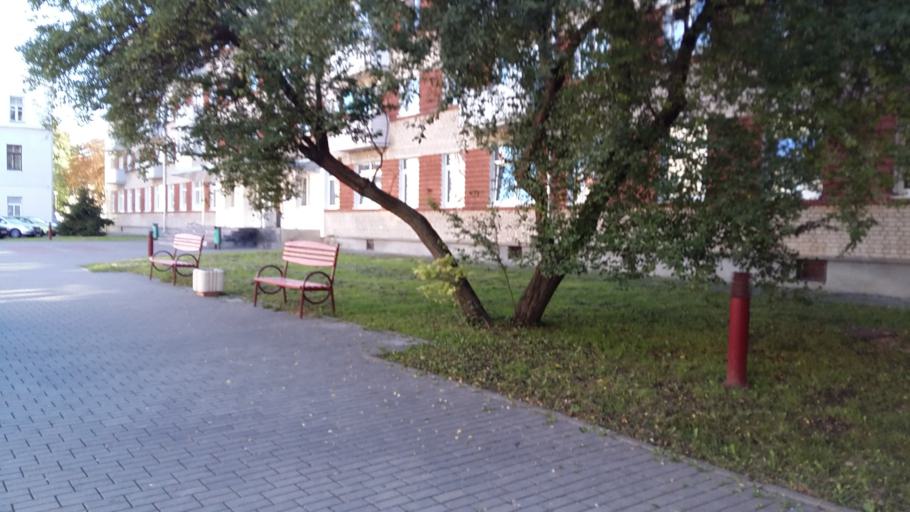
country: BY
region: Grodnenskaya
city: Hrodna
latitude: 53.6765
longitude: 23.8334
